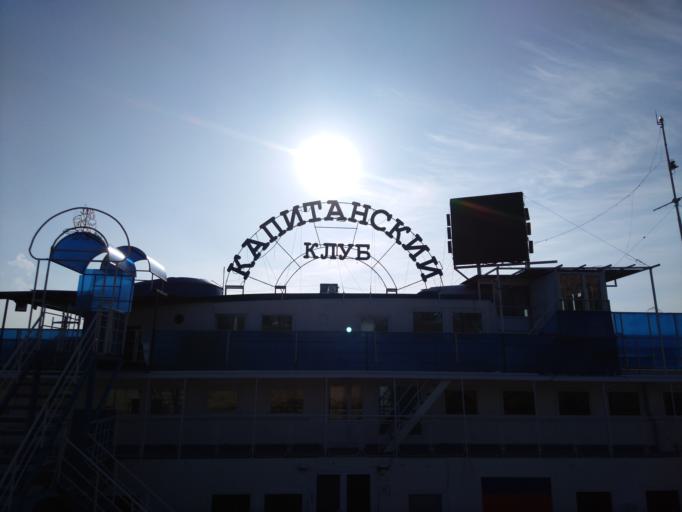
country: RU
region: Krasnoyarskiy
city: Krasnoyarsk
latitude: 56.0059
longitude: 92.8682
